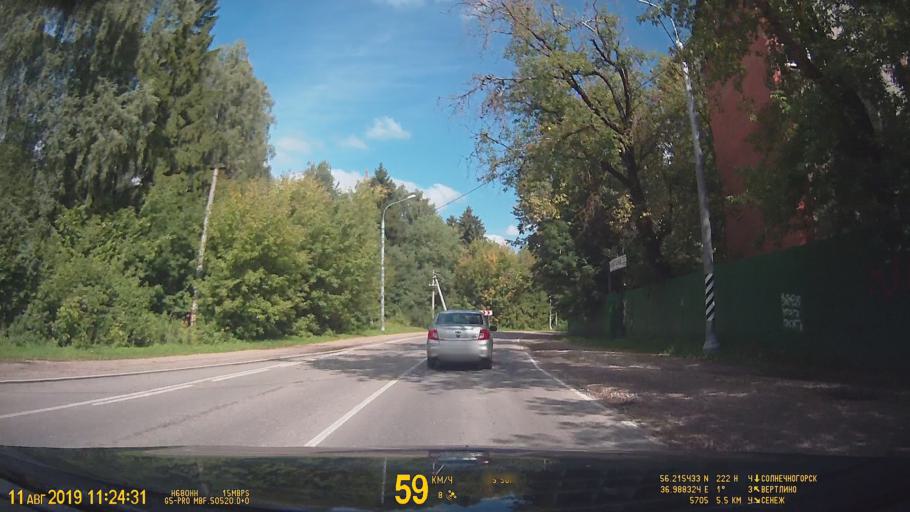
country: RU
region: Moskovskaya
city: Solnechnogorsk
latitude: 56.2156
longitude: 36.9883
